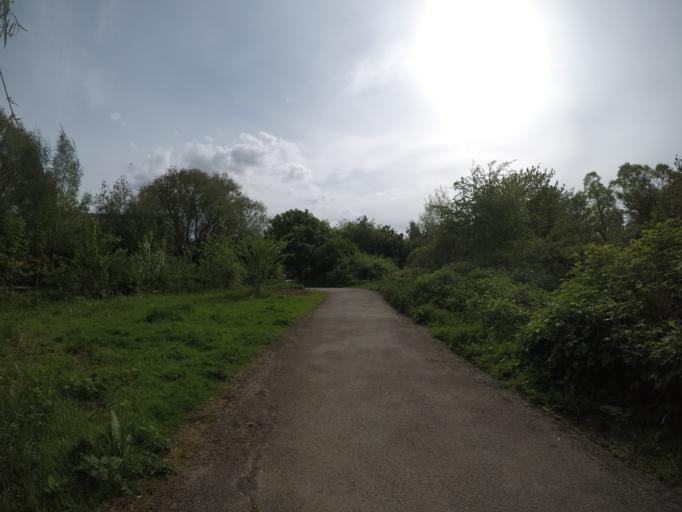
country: GB
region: England
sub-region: City of York
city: Heslington
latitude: 53.9569
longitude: -1.0627
